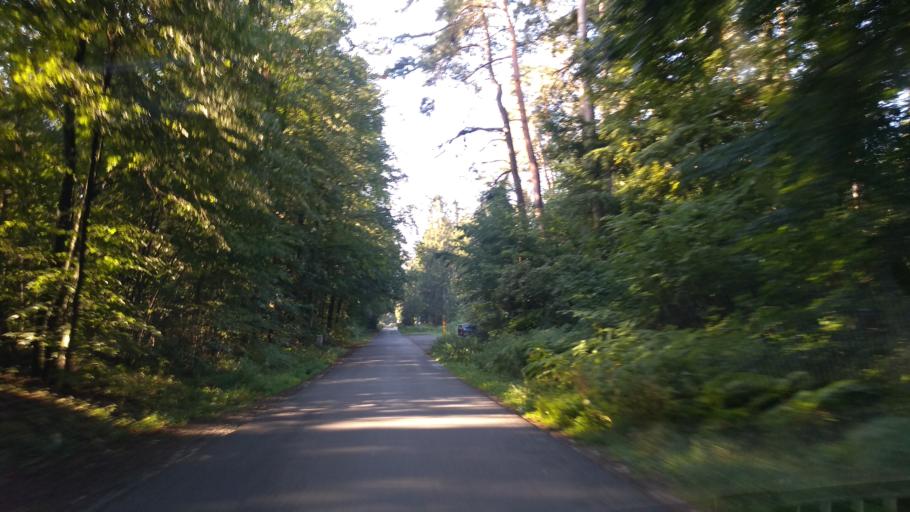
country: DE
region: North Rhine-Westphalia
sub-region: Regierungsbezirk Koln
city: Stossdorf
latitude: 50.8186
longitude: 7.2634
